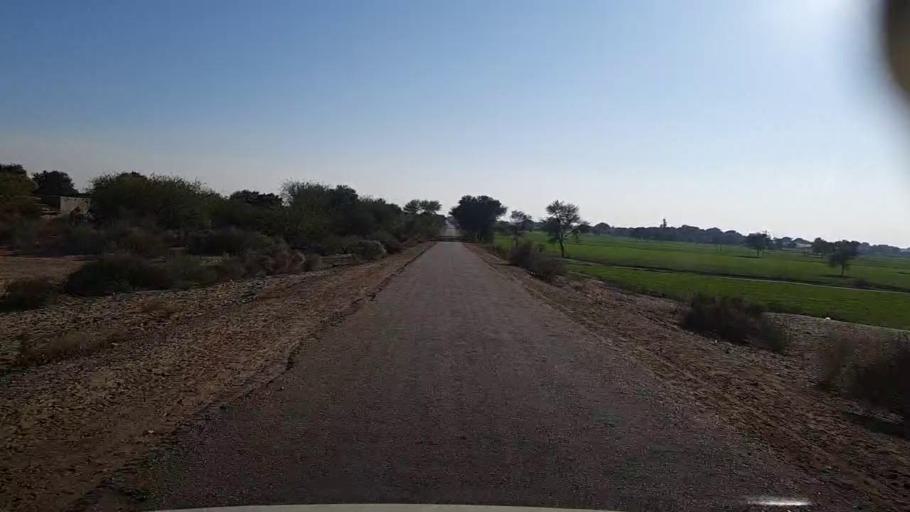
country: PK
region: Sindh
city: Khairpur
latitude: 27.8995
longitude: 69.7481
